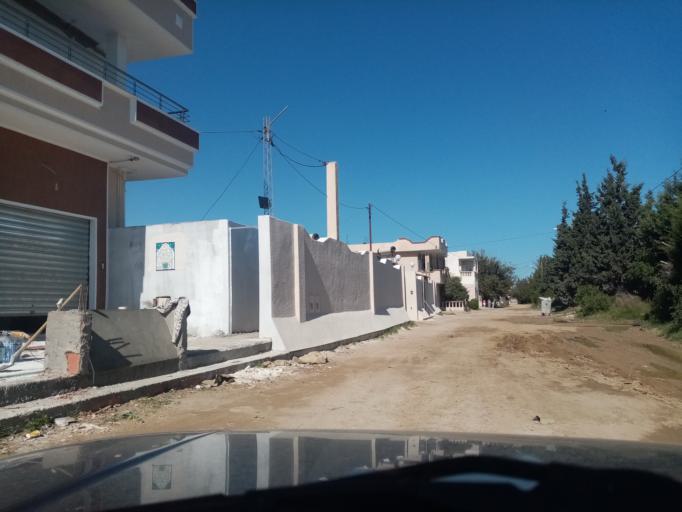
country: TN
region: Nabul
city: Bu `Urqub
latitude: 36.5762
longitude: 10.5720
